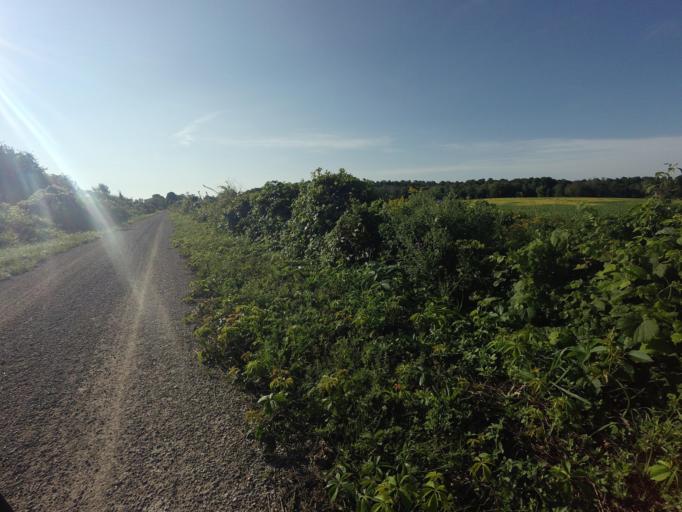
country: CA
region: Ontario
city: Goderich
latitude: 43.7532
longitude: -81.5083
